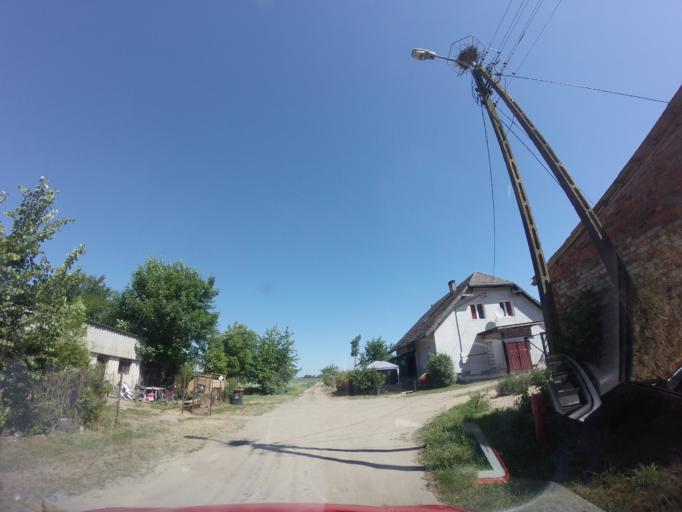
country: PL
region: West Pomeranian Voivodeship
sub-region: Powiat choszczenski
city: Choszczno
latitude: 53.2290
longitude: 15.3863
